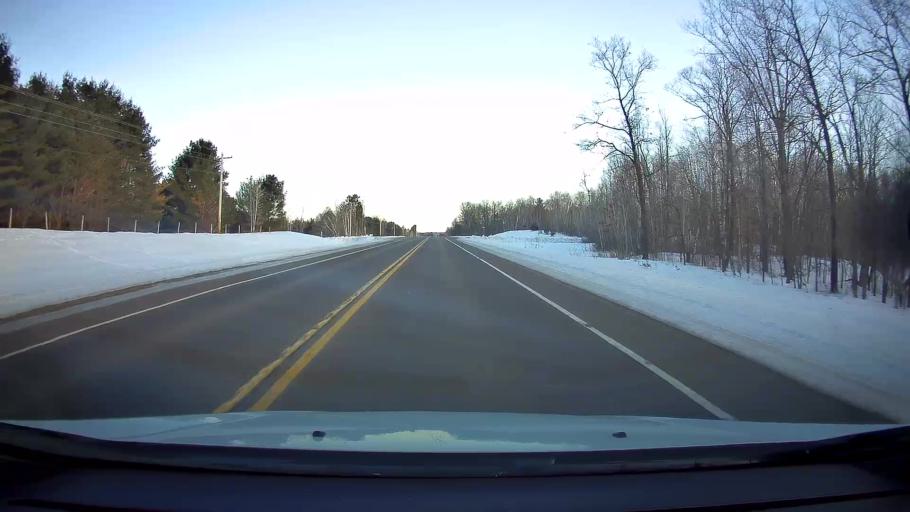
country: US
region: Wisconsin
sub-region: Barron County
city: Cumberland
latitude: 45.5877
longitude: -92.0176
